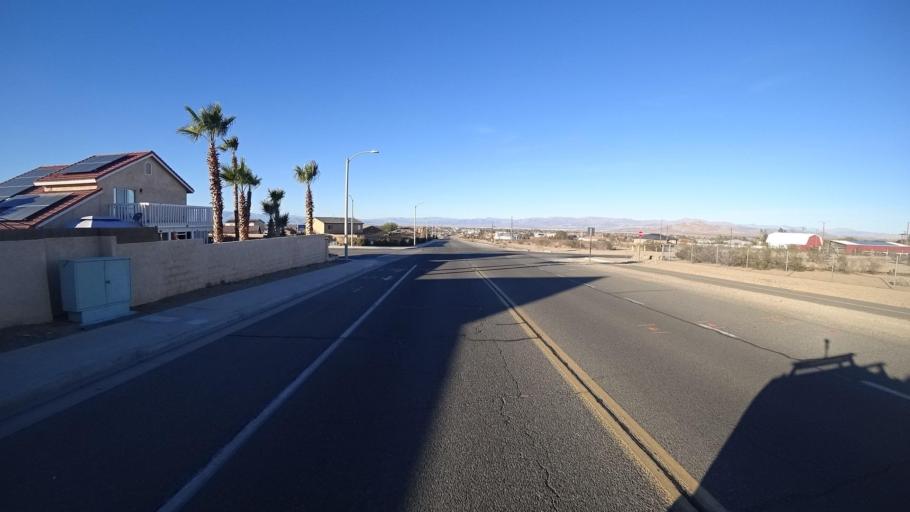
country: US
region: California
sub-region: Kern County
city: Ridgecrest
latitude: 35.5858
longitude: -117.6704
